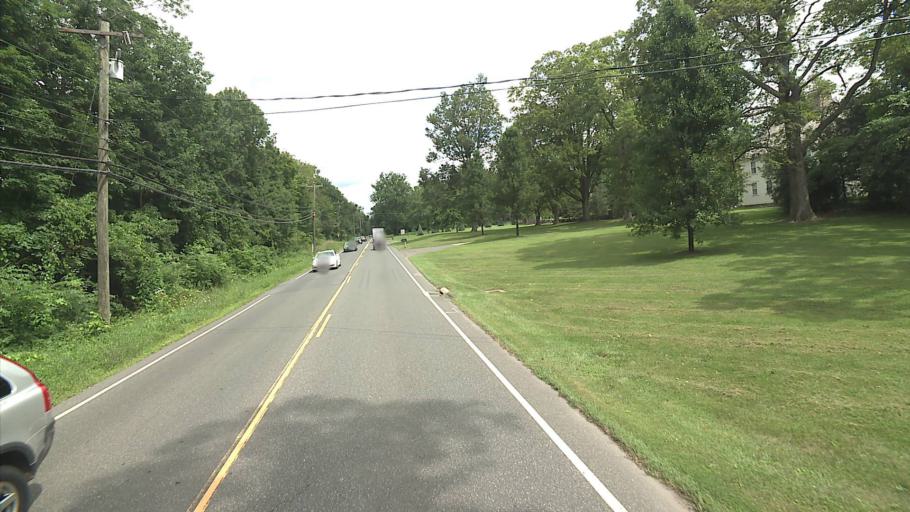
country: US
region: Connecticut
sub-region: New Haven County
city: Southbury
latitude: 41.4903
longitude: -73.2131
